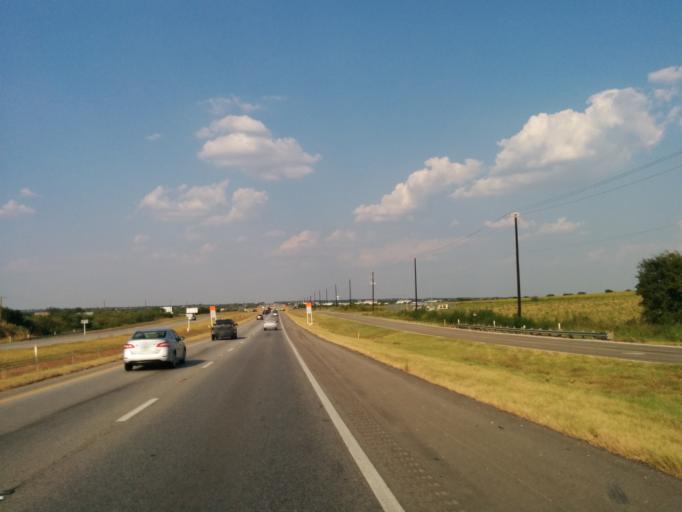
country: US
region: Texas
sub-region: Bexar County
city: Converse
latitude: 29.4687
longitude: -98.2807
